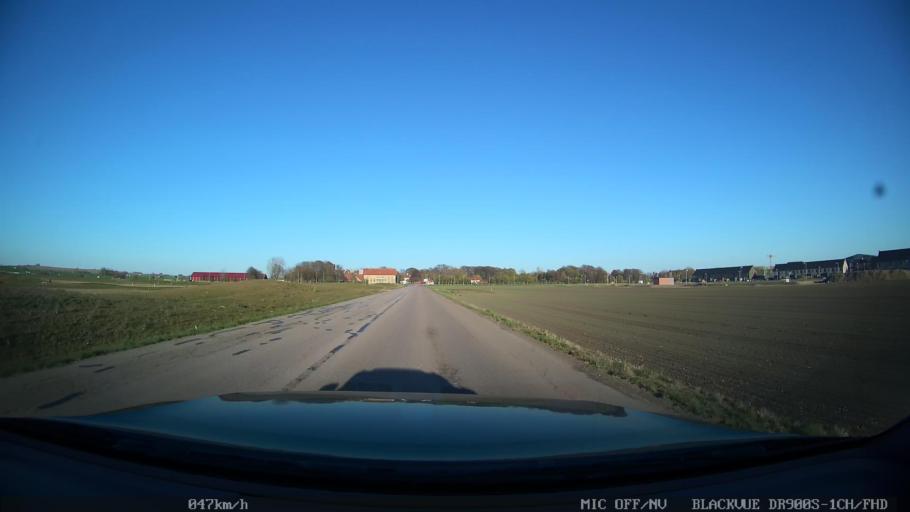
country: SE
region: Skane
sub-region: Landskrona
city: Landskrona
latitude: 55.9031
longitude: 12.8192
